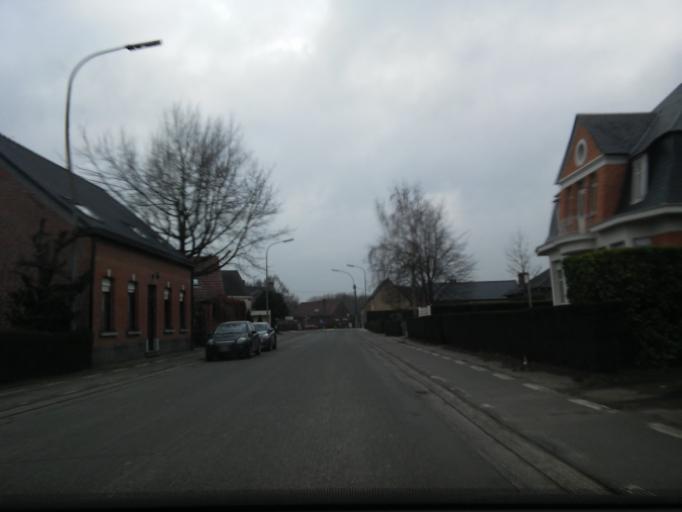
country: BE
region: Flanders
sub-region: Provincie Oost-Vlaanderen
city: Wetteren
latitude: 51.0283
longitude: 3.8905
